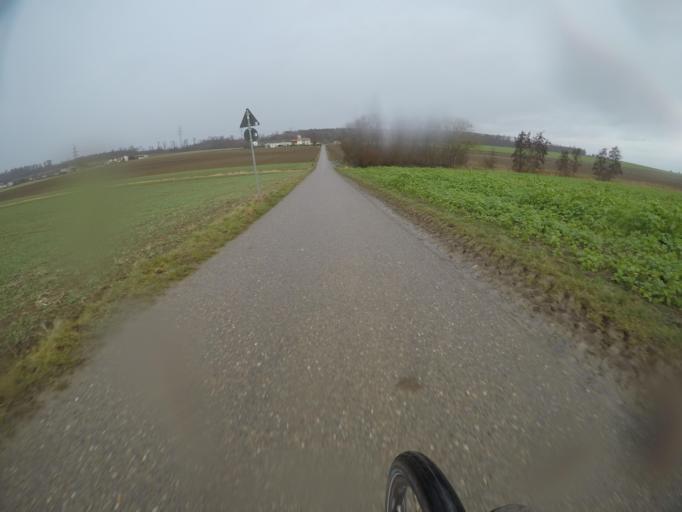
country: DE
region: Baden-Wuerttemberg
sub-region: Regierungsbezirk Stuttgart
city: Hemmingen
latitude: 48.8671
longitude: 9.0108
